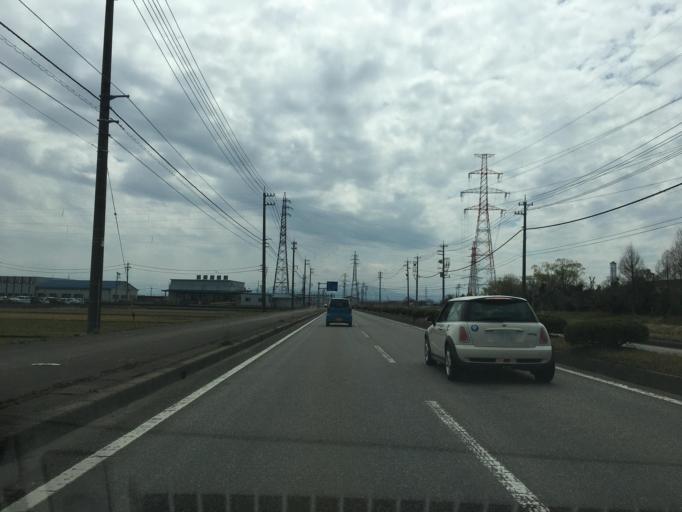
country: JP
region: Toyama
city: Kuragaki-kosugi
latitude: 36.7499
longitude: 137.1304
